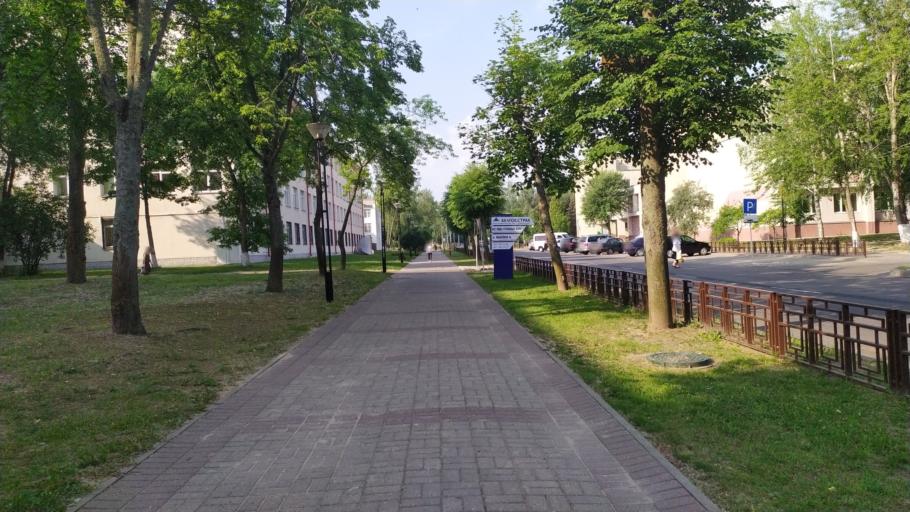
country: BY
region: Vitebsk
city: Navapolatsk
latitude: 55.5328
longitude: 28.6468
